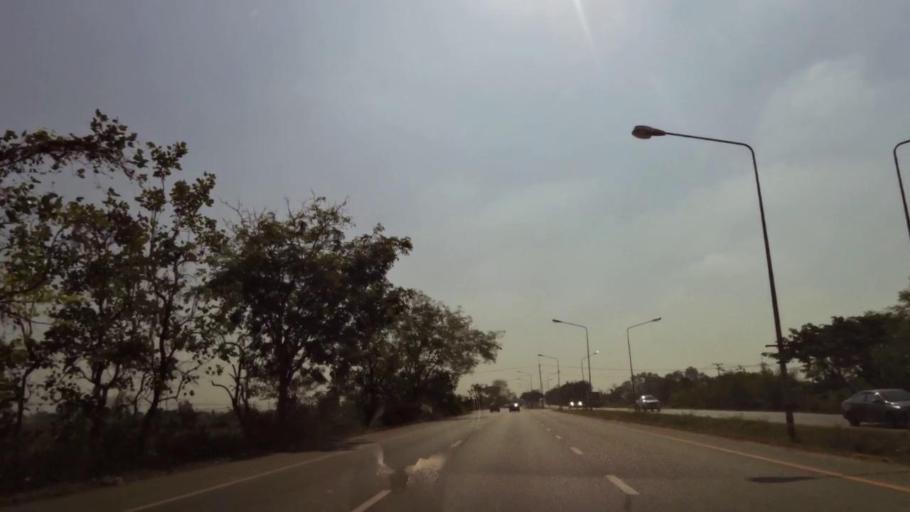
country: TH
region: Phichit
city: Wachira Barami
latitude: 16.4715
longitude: 100.1473
